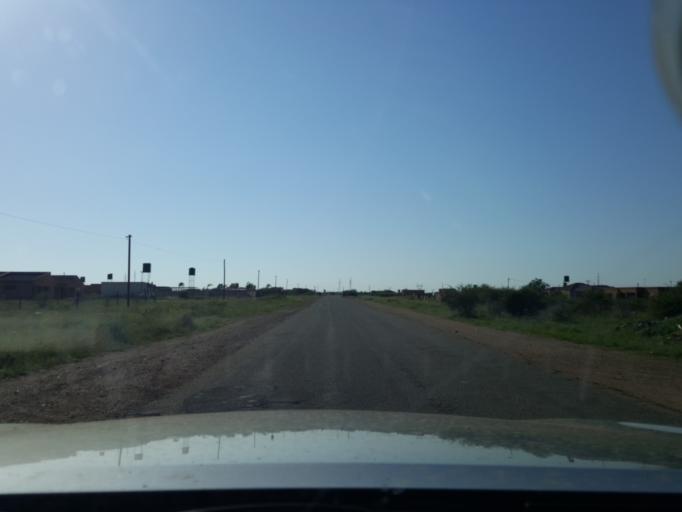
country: ZA
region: North-West
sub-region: Ngaka Modiri Molema District Municipality
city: Mmabatho
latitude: -25.8367
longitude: 25.6678
